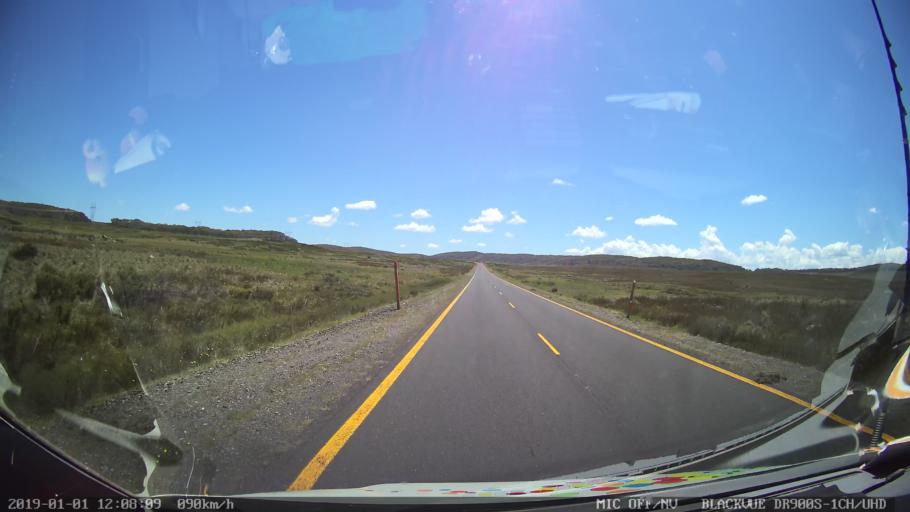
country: AU
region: New South Wales
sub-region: Tumut Shire
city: Tumut
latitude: -35.8240
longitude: 148.4933
